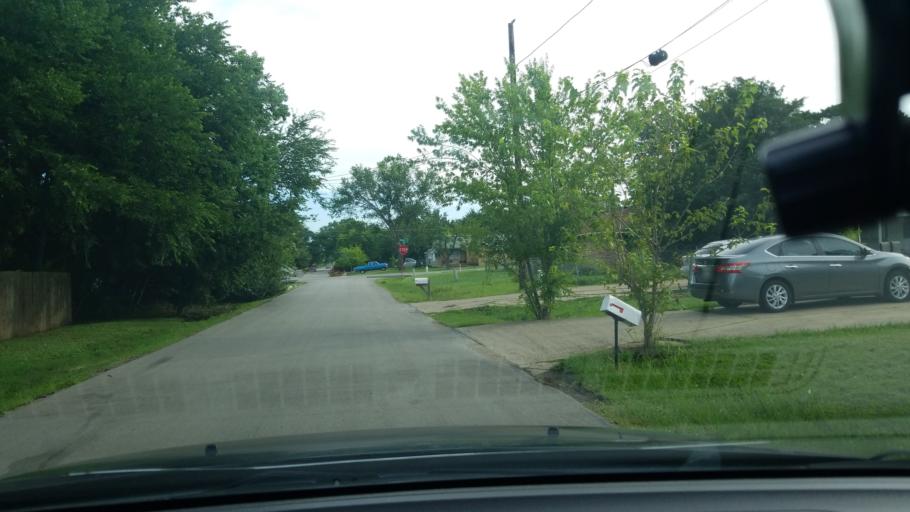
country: US
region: Texas
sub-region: Dallas County
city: Balch Springs
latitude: 32.7586
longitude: -96.6618
